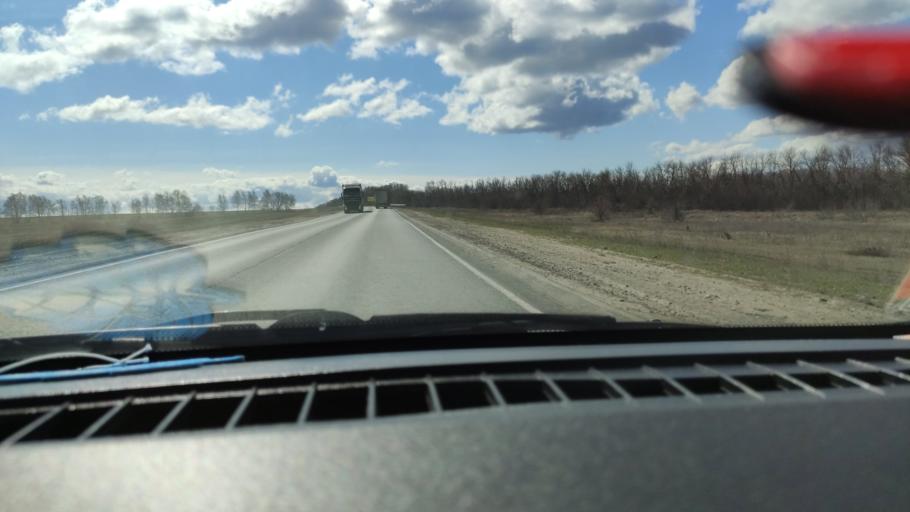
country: RU
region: Saratov
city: Dukhovnitskoye
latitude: 52.7267
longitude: 48.2601
